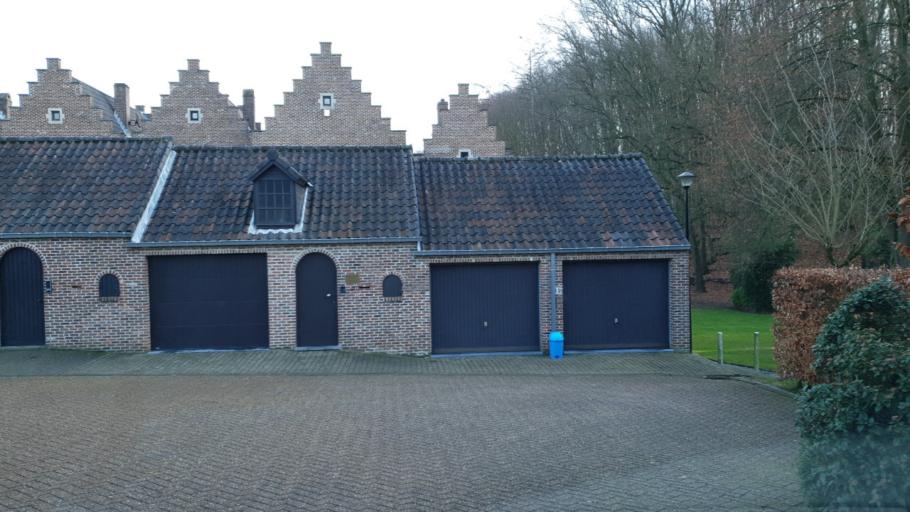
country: BE
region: Flanders
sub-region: Provincie Vlaams-Brabant
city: Kortenberg
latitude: 50.8747
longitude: 4.5378
